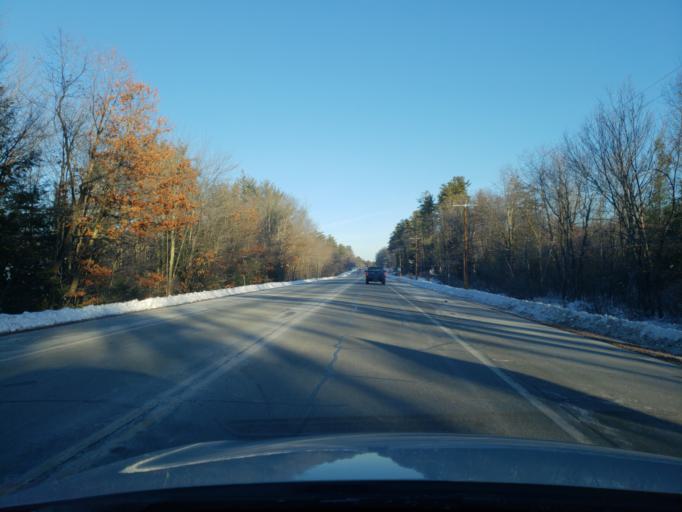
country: US
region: New Hampshire
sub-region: Hillsborough County
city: Pinardville
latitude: 42.9853
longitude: -71.5217
